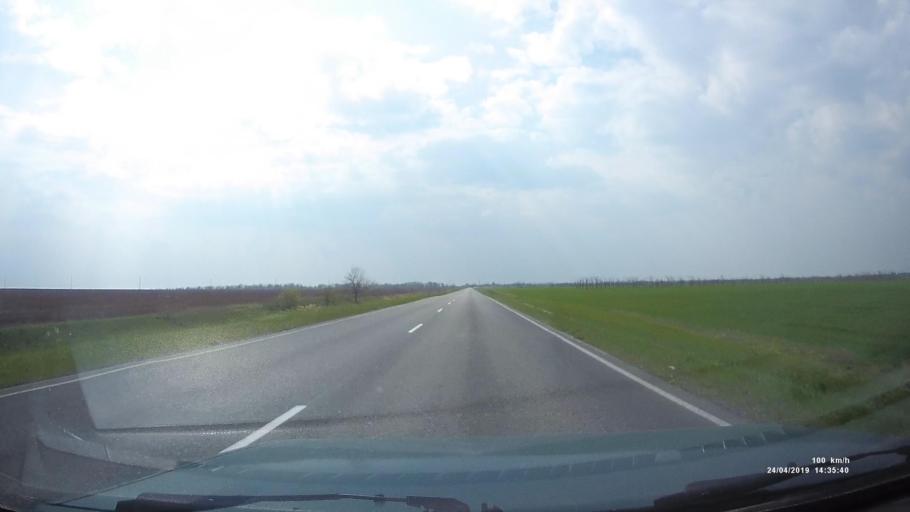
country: RU
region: Rostov
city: Remontnoye
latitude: 46.3739
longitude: 43.9060
